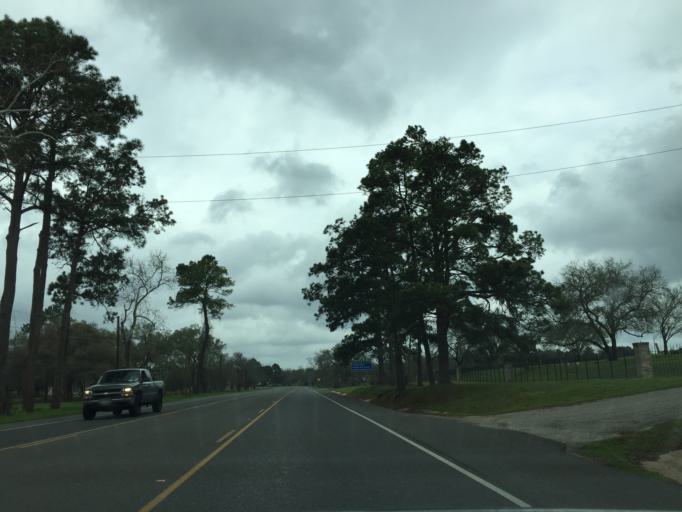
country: US
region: Texas
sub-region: Bastrop County
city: Bastrop
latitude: 30.1149
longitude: -97.3078
